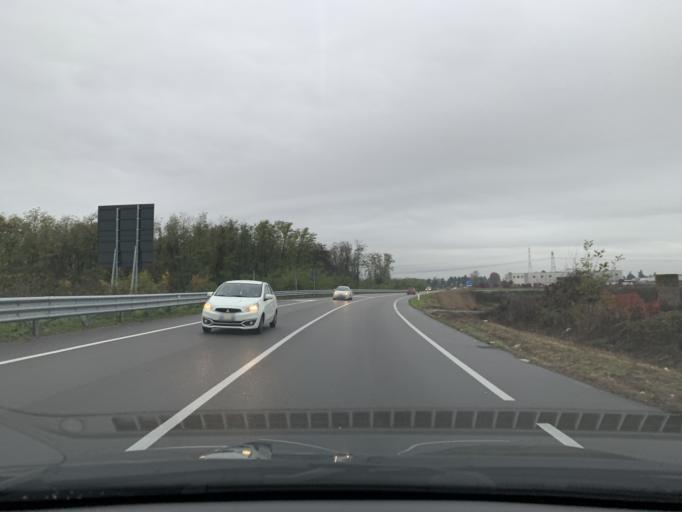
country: IT
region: Lombardy
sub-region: Provincia di Como
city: Rovello Porro
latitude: 45.6529
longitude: 9.0524
